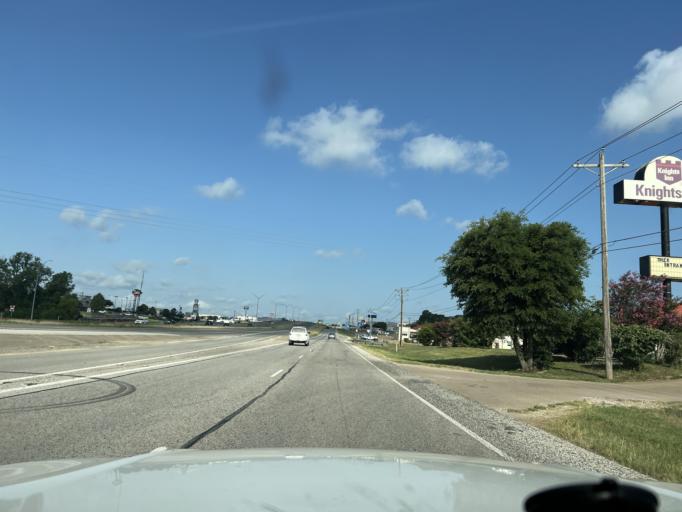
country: US
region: Texas
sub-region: Washington County
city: Brenham
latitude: 30.1429
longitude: -96.3888
